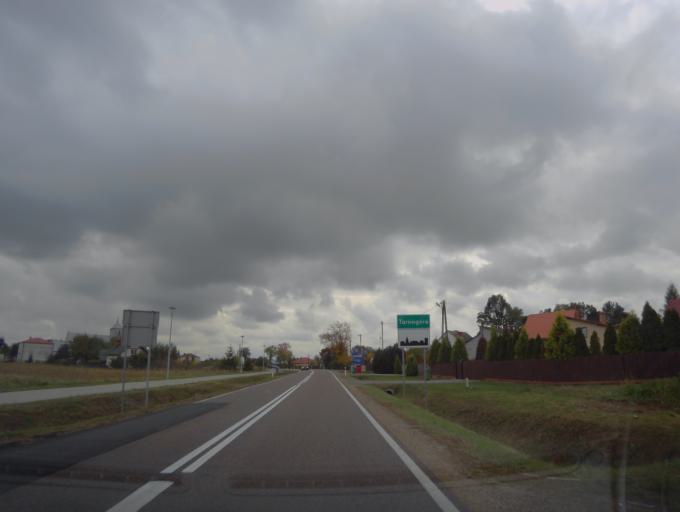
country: PL
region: Subcarpathian Voivodeship
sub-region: Powiat nizanski
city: Krzeszow
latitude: 50.3716
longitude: 22.3143
